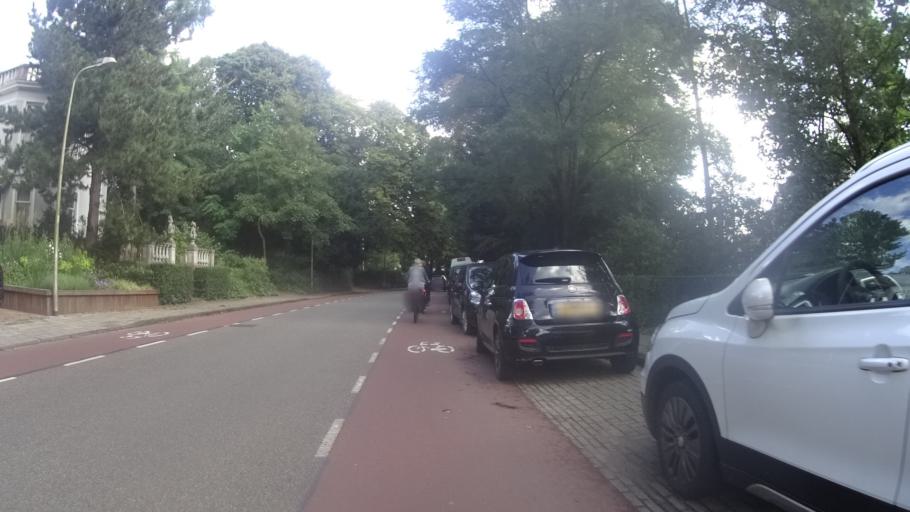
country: NL
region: North Holland
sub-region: Gemeente Bloemendaal
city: Bloemendaal
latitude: 52.3930
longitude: 4.6097
